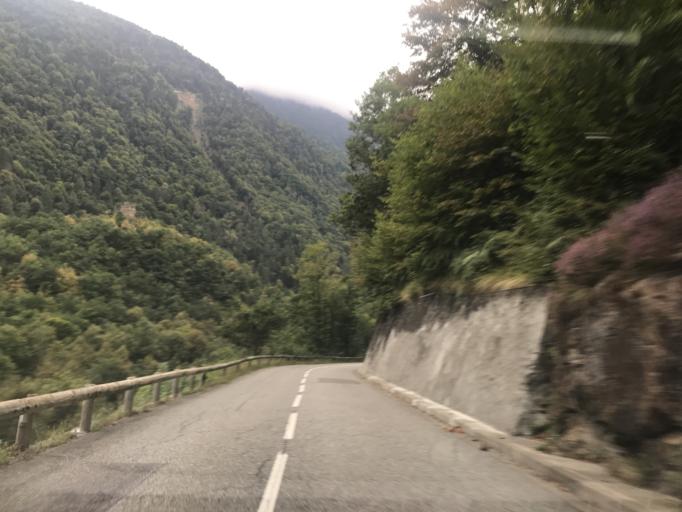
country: FR
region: Midi-Pyrenees
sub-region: Departement de la Haute-Garonne
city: Bagneres-de-Luchon
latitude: 42.7682
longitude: 0.6133
